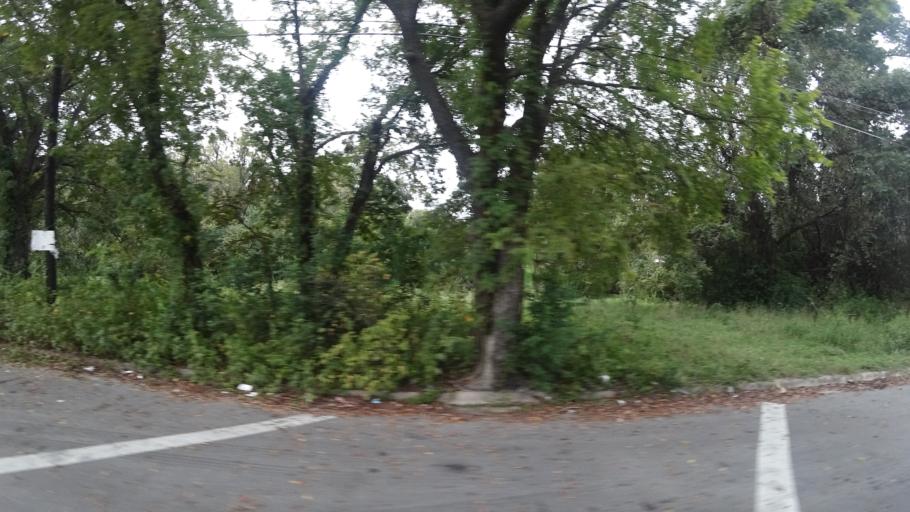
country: US
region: Texas
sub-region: Travis County
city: Wells Branch
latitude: 30.3493
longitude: -97.6889
